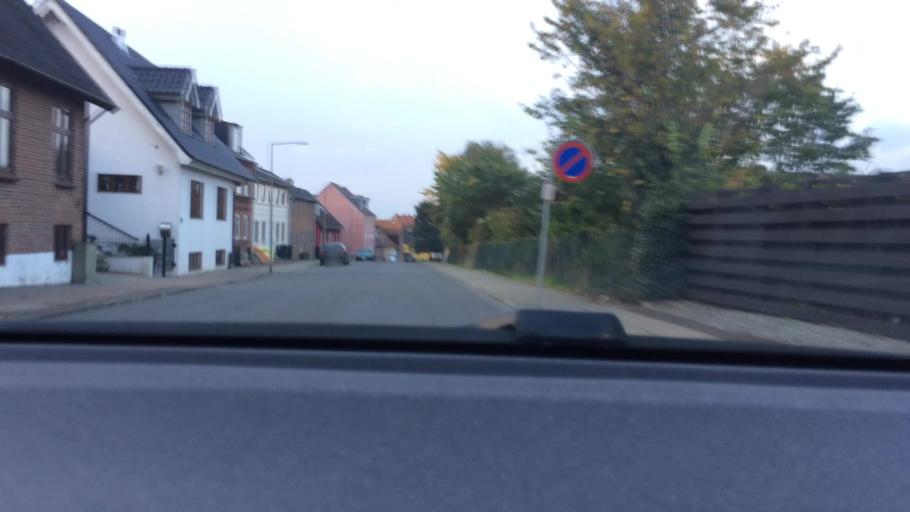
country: DK
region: Central Jutland
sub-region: Horsens Kommune
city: Horsens
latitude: 55.8714
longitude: 9.8463
